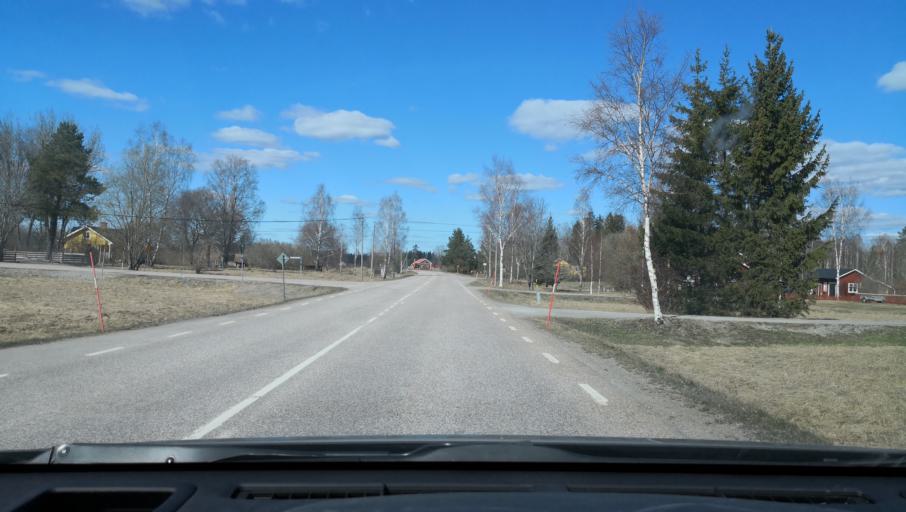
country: SE
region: Vaestmanland
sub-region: Sala Kommun
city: Sala
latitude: 59.9859
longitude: 16.6446
